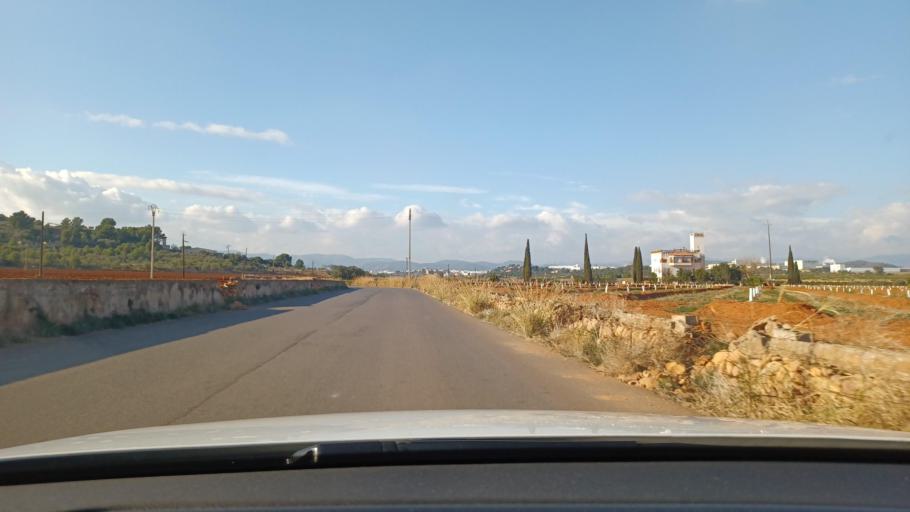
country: ES
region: Valencia
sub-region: Provincia de Castello
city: Betxi
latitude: 39.9433
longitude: -0.2145
